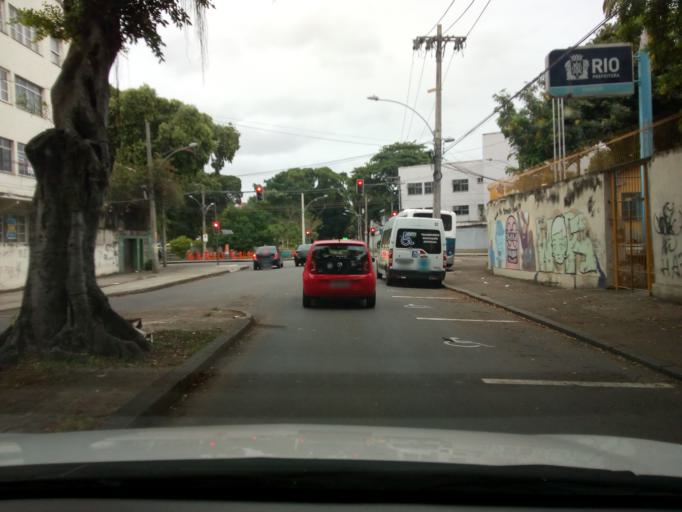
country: BR
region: Rio de Janeiro
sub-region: Rio De Janeiro
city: Rio de Janeiro
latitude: -22.9134
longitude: -43.2266
